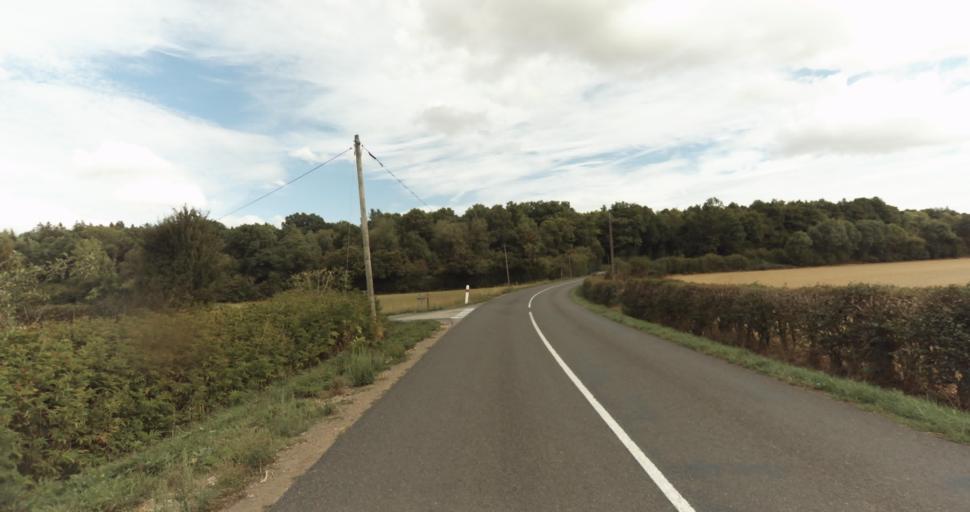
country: FR
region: Lower Normandy
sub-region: Departement du Calvados
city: Orbec
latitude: 48.8991
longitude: 0.3735
